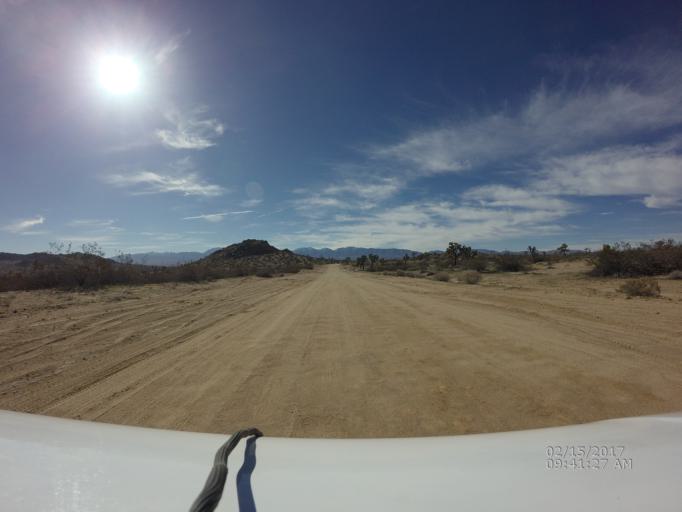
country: US
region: California
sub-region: Los Angeles County
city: Lake Los Angeles
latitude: 34.6197
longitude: -117.8899
